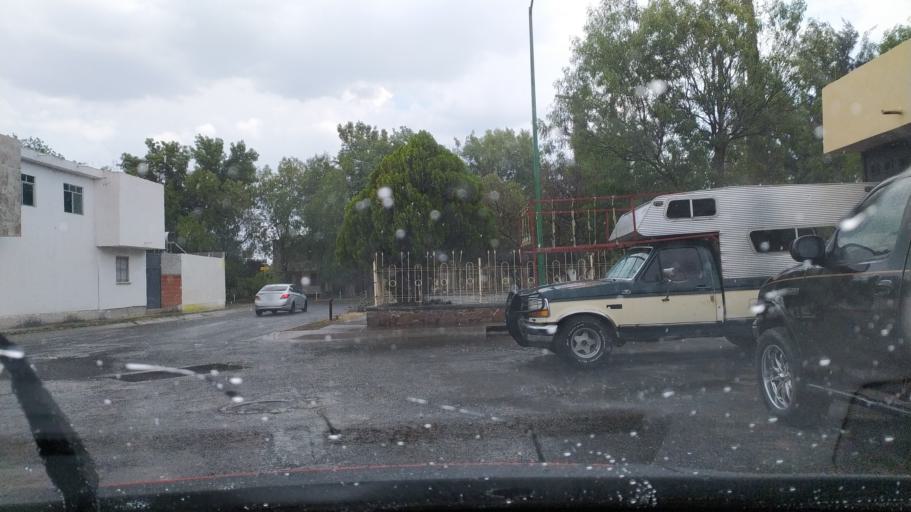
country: MX
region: Guanajuato
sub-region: San Francisco del Rincon
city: Estacion de San Francisco
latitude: 21.0276
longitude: -101.8291
